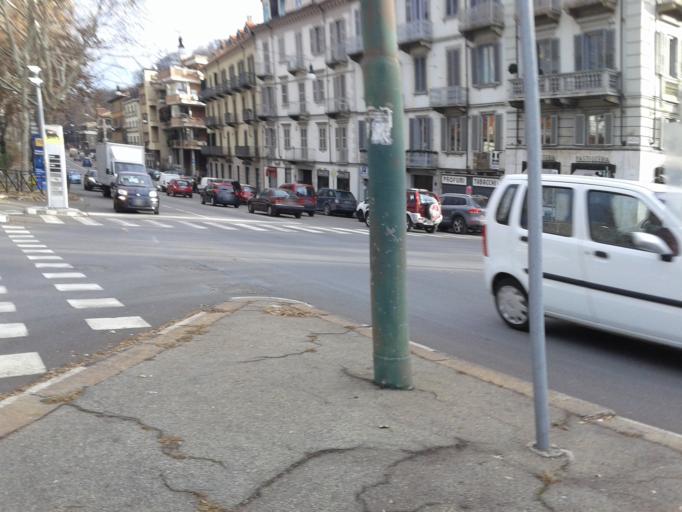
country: IT
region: Piedmont
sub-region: Provincia di Torino
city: Turin
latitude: 45.0578
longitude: 7.6932
